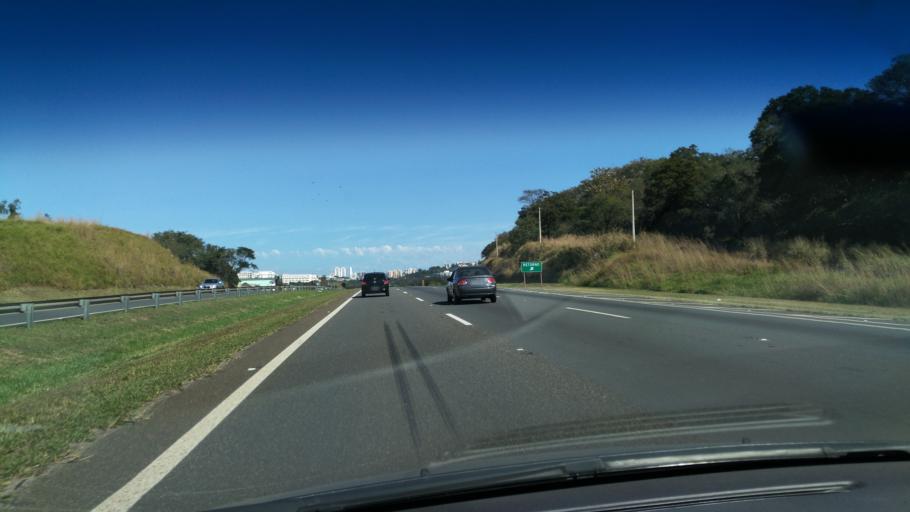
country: BR
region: Sao Paulo
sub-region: Campinas
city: Campinas
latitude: -22.8093
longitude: -47.0341
